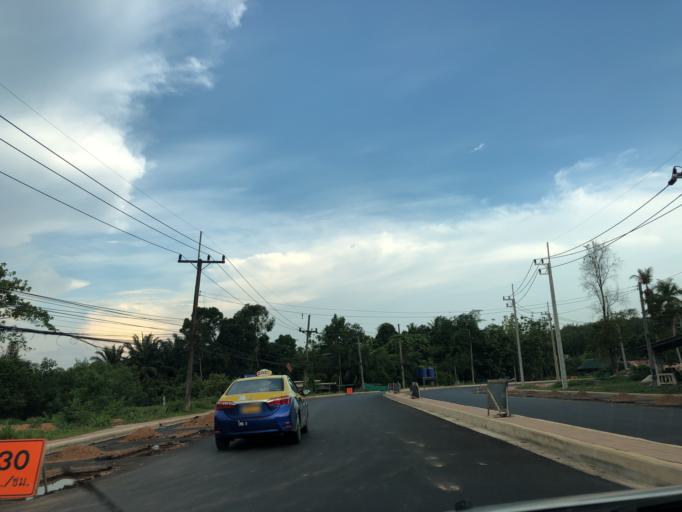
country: TH
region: Phangnga
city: Ban Ao Nang
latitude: 8.0667
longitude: 98.8433
